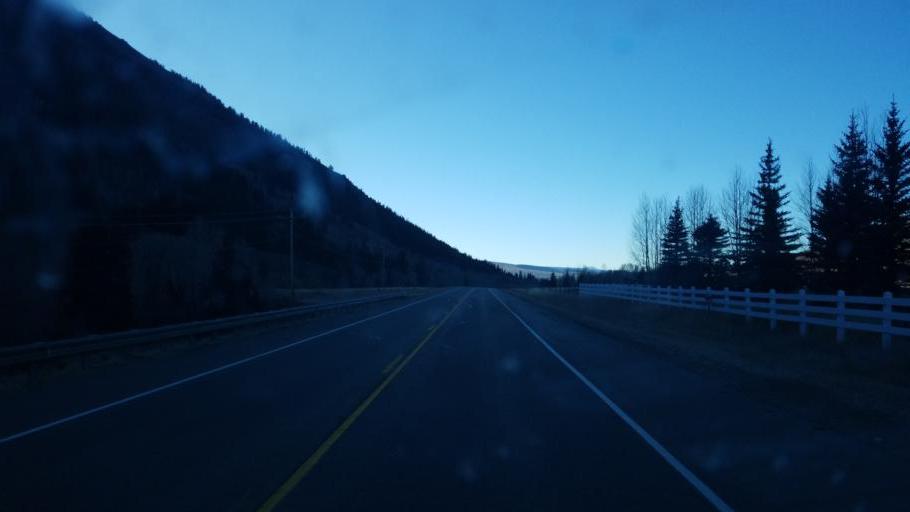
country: US
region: Colorado
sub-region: Gunnison County
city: Crested Butte
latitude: 38.7891
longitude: -106.8734
